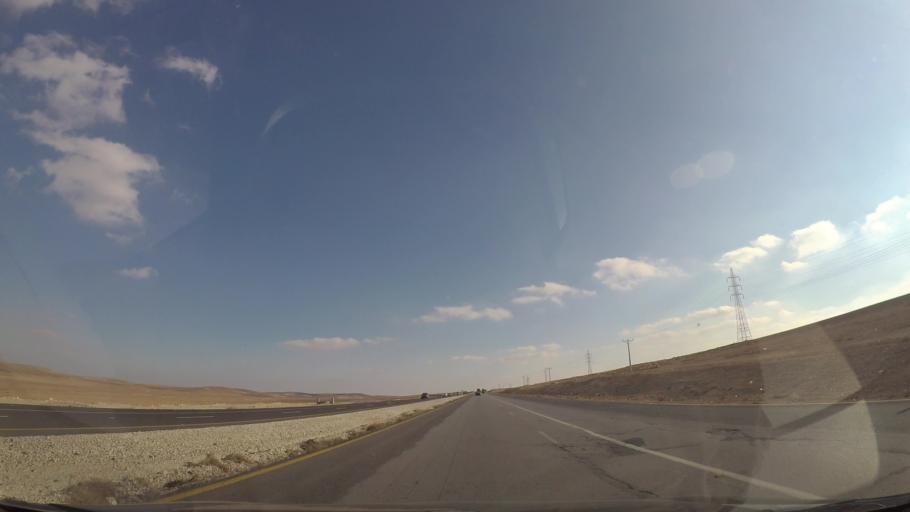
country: JO
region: Karak
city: Karak City
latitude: 31.1519
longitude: 36.0246
